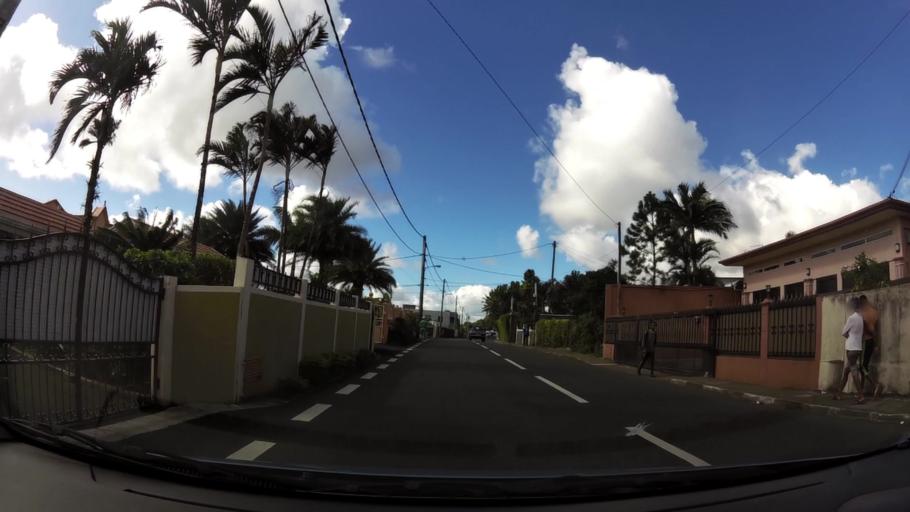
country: MU
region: Plaines Wilhems
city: Curepipe
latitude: -20.3277
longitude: 57.5271
